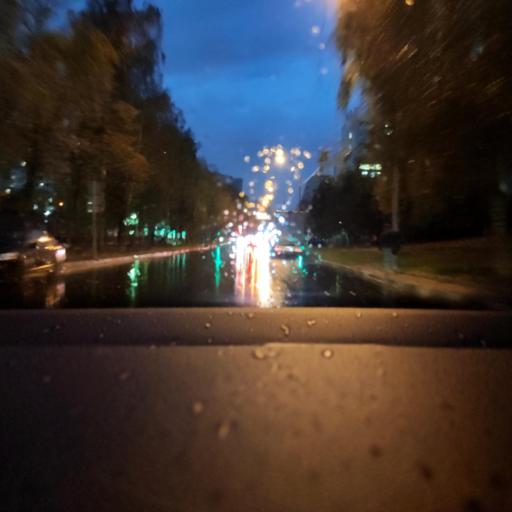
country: RU
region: Moskovskaya
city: Razvilka
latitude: 55.6026
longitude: 37.7359
